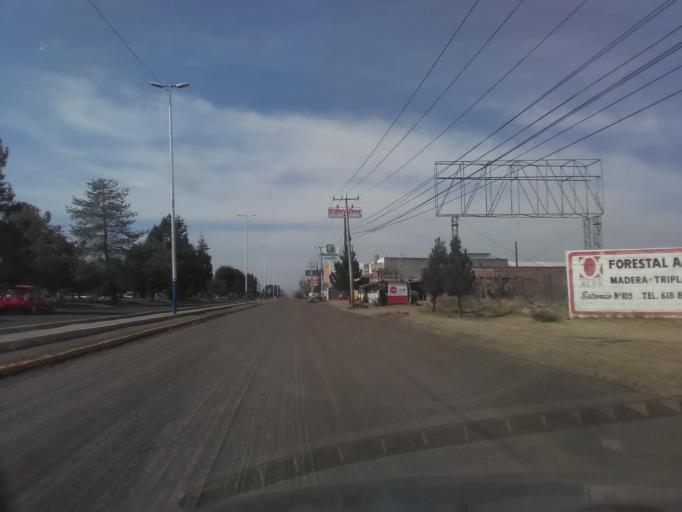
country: MX
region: Durango
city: Victoria de Durango
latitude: 24.0571
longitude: -104.6128
